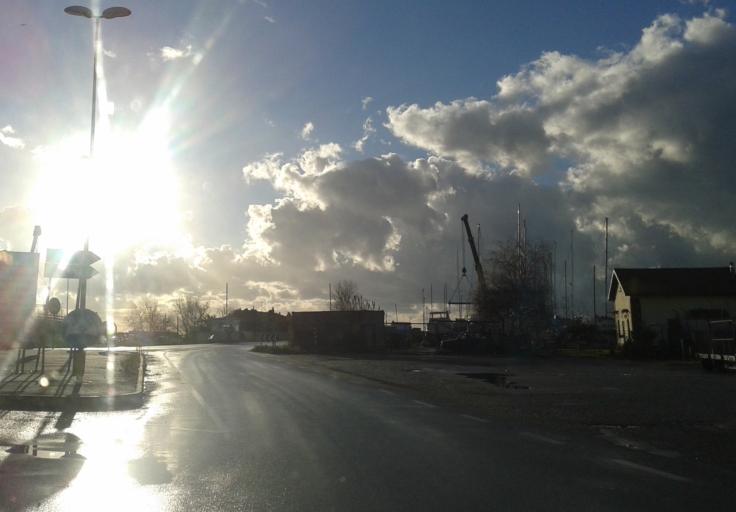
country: IT
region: Tuscany
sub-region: Provincia di Livorno
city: Livorno
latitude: 43.5841
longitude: 10.3063
